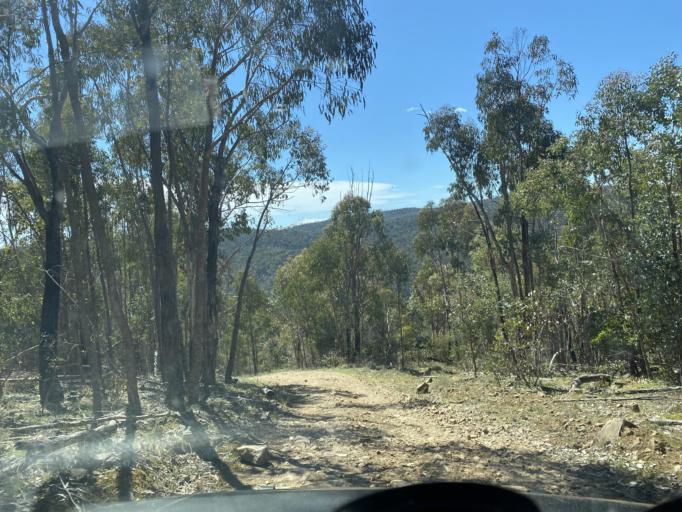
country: AU
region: Victoria
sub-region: Benalla
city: Benalla
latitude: -36.7210
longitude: 146.1820
